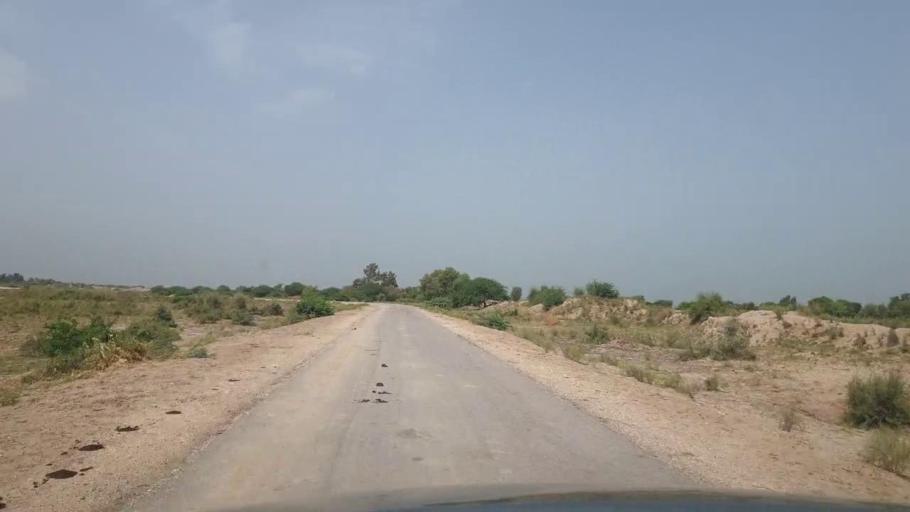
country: PK
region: Sindh
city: Madeji
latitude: 27.8397
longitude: 68.4336
